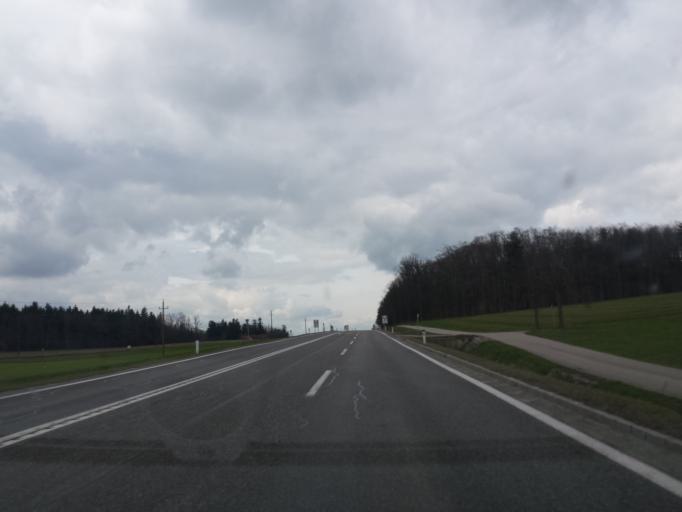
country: AT
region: Lower Austria
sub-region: Politischer Bezirk Krems
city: Gfohl
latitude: 48.5028
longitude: 15.5311
